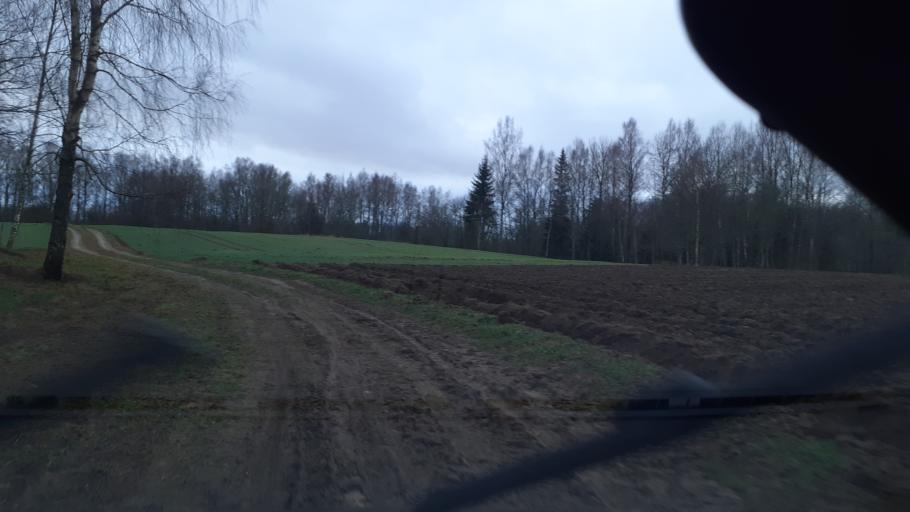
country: LV
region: Kuldigas Rajons
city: Kuldiga
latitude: 56.8857
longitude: 21.7690
